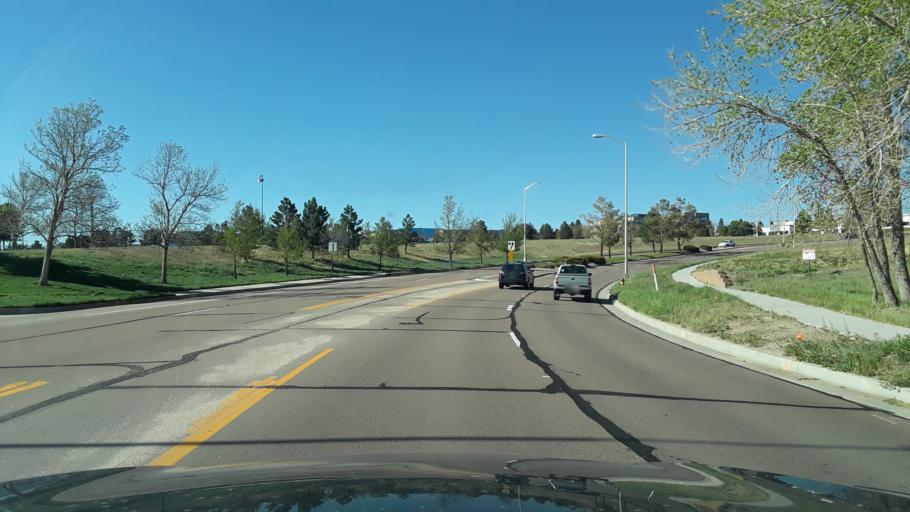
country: US
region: Colorado
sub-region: El Paso County
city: Air Force Academy
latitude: 38.9549
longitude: -104.7920
